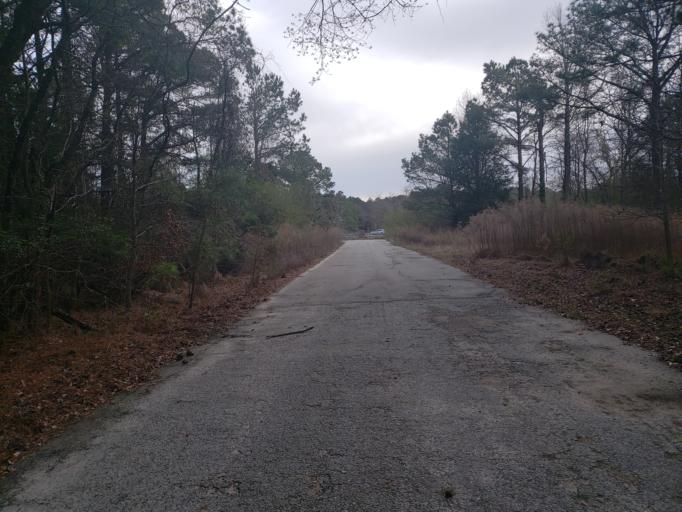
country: US
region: Virginia
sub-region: City of Newport News
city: Newport News
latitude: 36.8988
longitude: -76.4264
